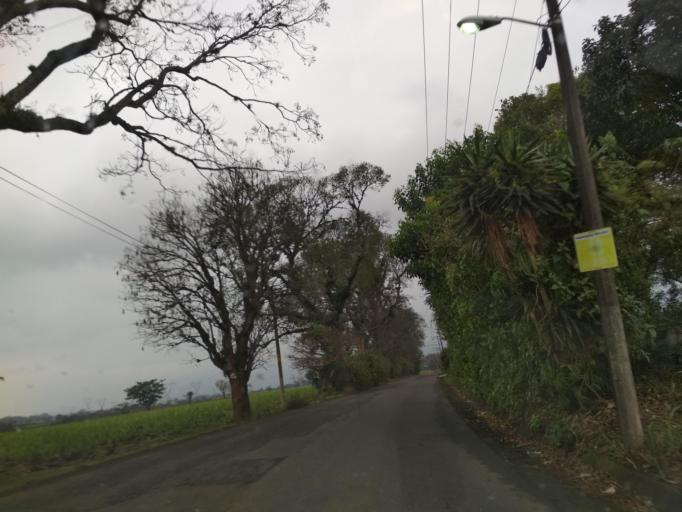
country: MX
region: Veracruz
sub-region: Cordoba
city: Veinte de Noviembre
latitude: 18.8593
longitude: -96.9516
